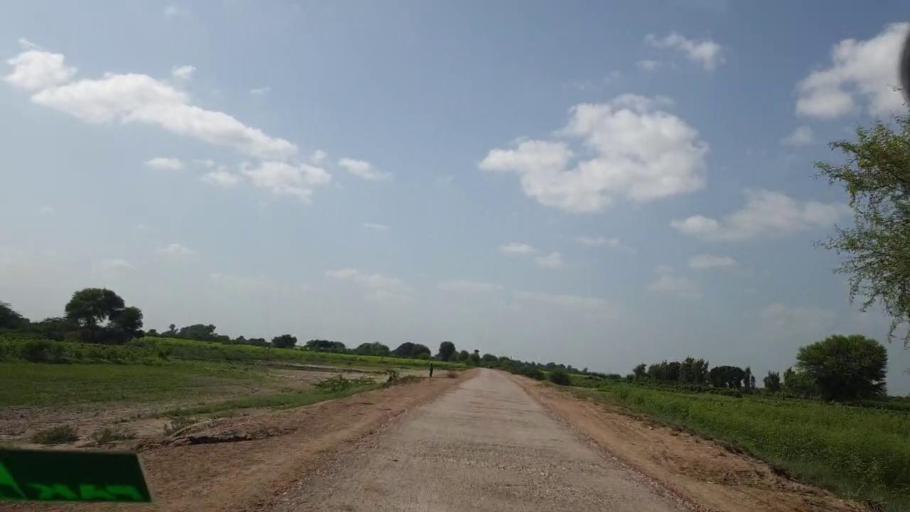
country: PK
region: Sindh
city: Naukot
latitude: 24.6512
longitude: 69.2183
